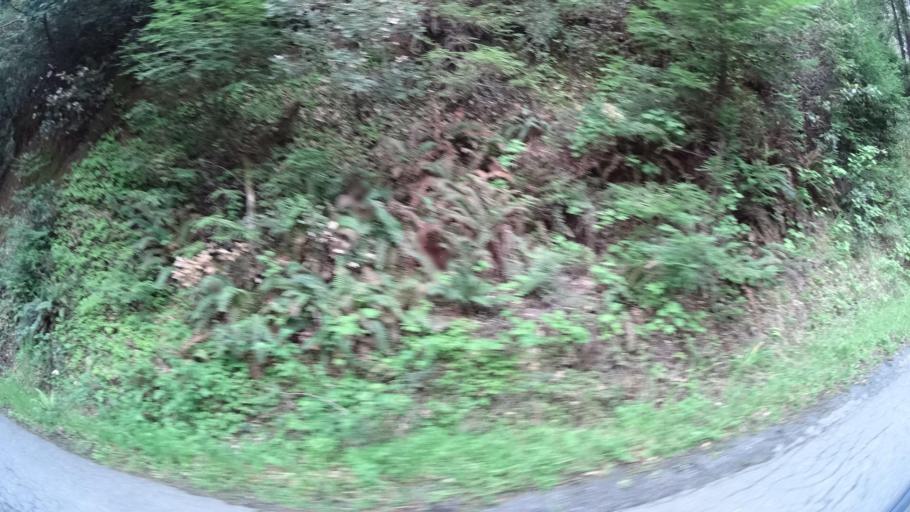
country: US
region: California
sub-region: Humboldt County
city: Redway
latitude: 40.3337
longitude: -123.8497
